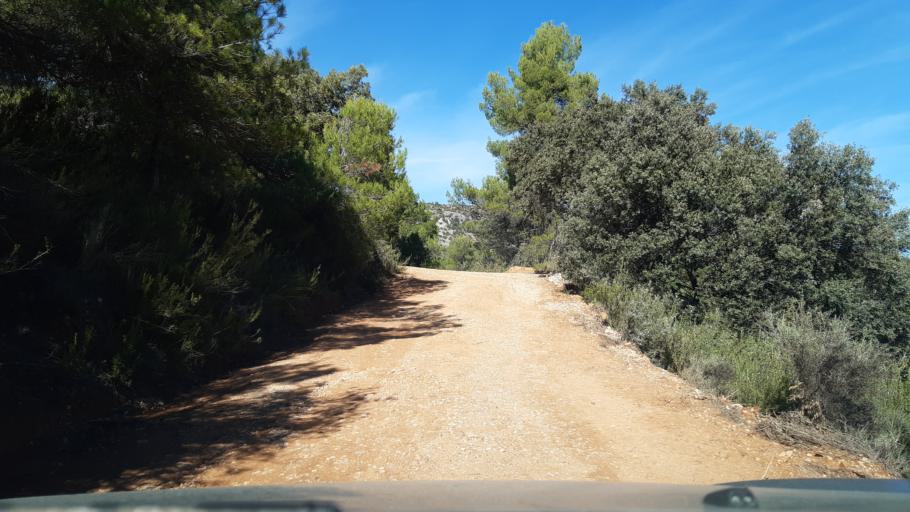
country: ES
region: Aragon
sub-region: Provincia de Teruel
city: Valderrobres
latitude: 40.8394
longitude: 0.2004
